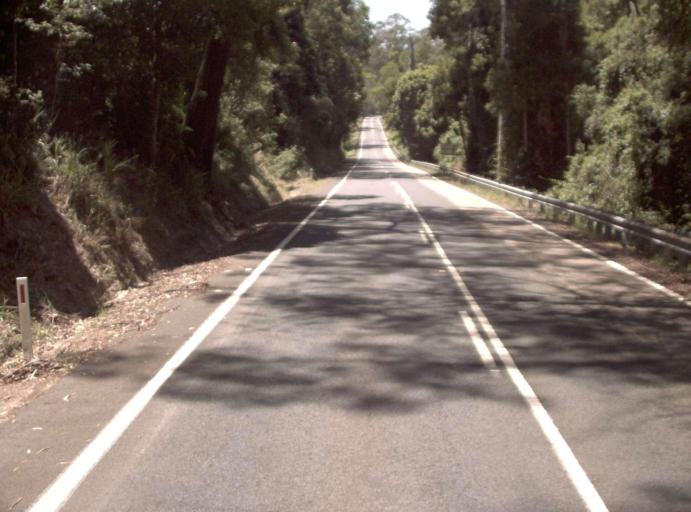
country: AU
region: Victoria
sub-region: East Gippsland
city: Lakes Entrance
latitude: -37.8067
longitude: 148.0403
